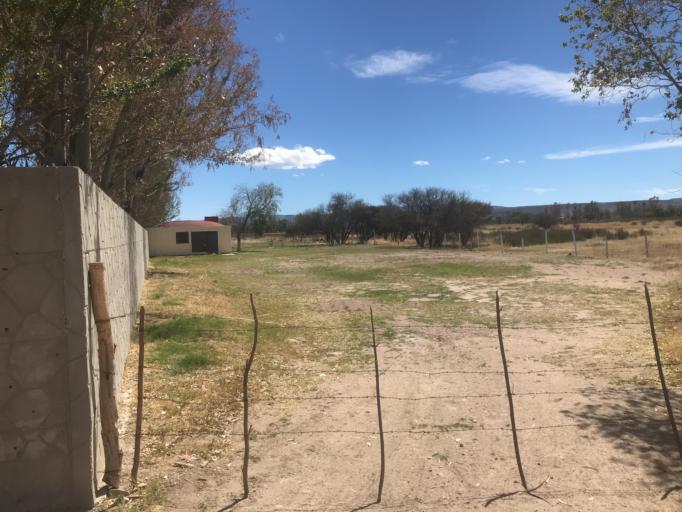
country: MX
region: Durango
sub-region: Durango
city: Sebastian Lerdo de Tejada
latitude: 23.9826
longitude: -104.6231
